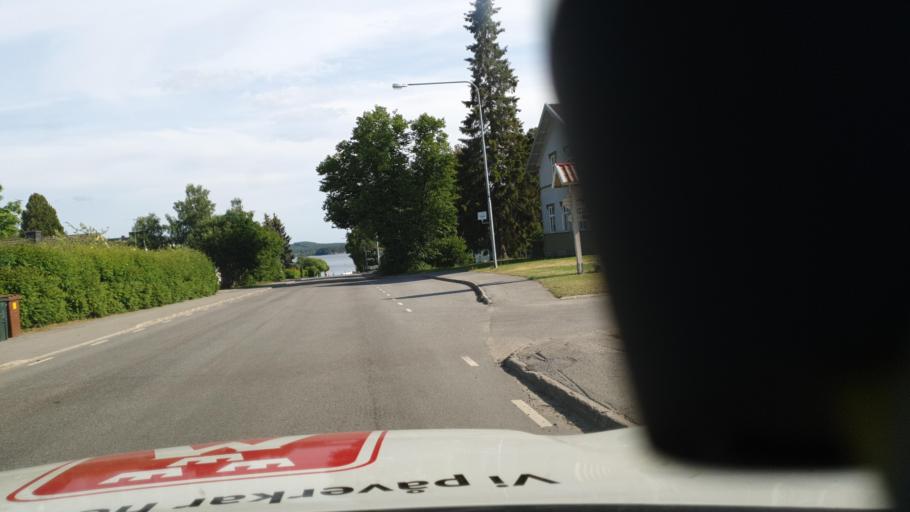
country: SE
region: Vaesterbotten
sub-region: Skelleftea Kommun
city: Burtraesk
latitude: 64.5195
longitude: 20.6568
